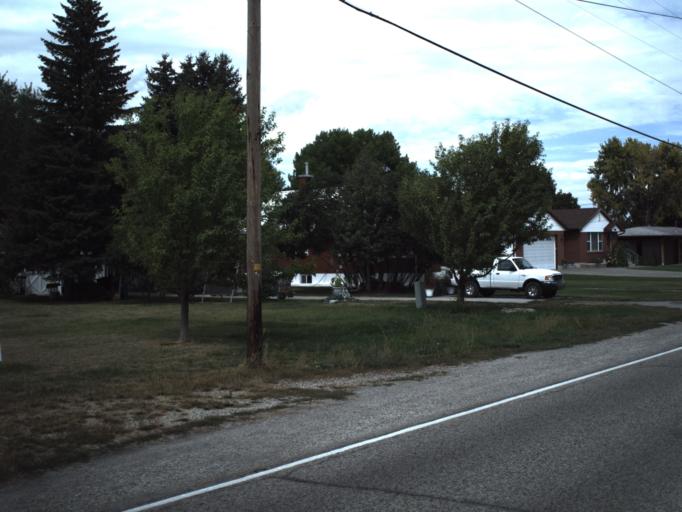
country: US
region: Utah
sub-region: Cache County
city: Wellsville
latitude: 41.6265
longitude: -111.9348
